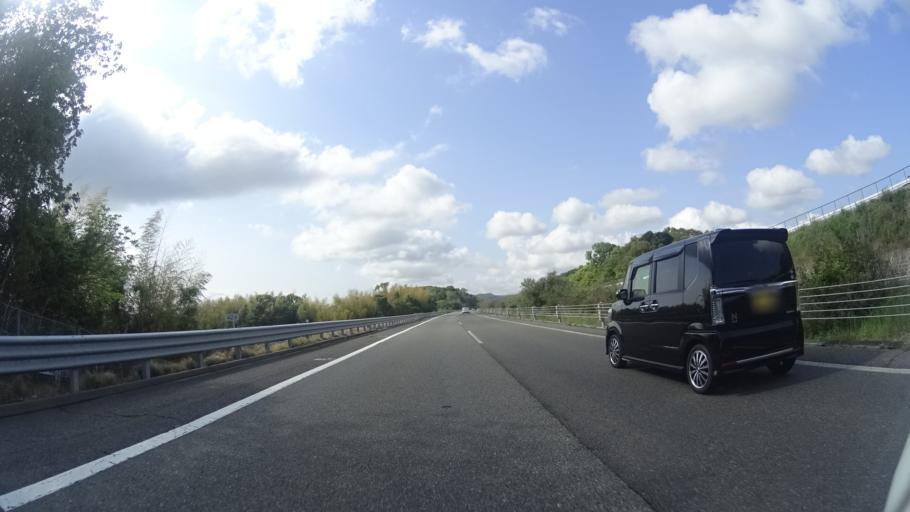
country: JP
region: Hyogo
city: Sumoto
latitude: 34.4569
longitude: 134.8780
